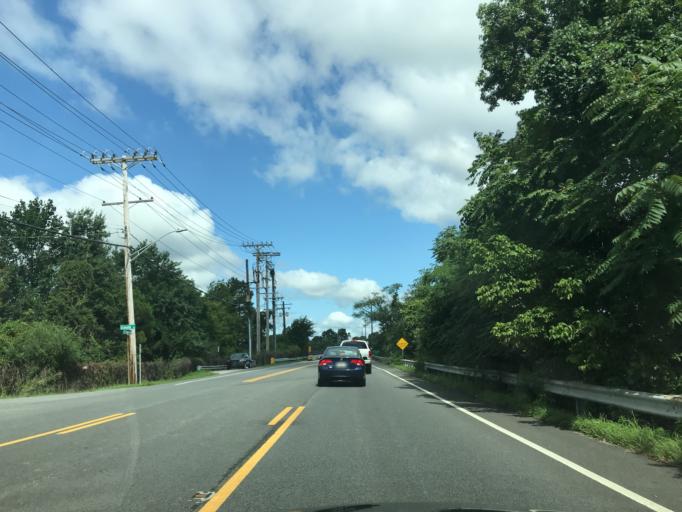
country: US
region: Maryland
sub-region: Anne Arundel County
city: Riviera Beach
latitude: 39.1618
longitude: -76.5226
